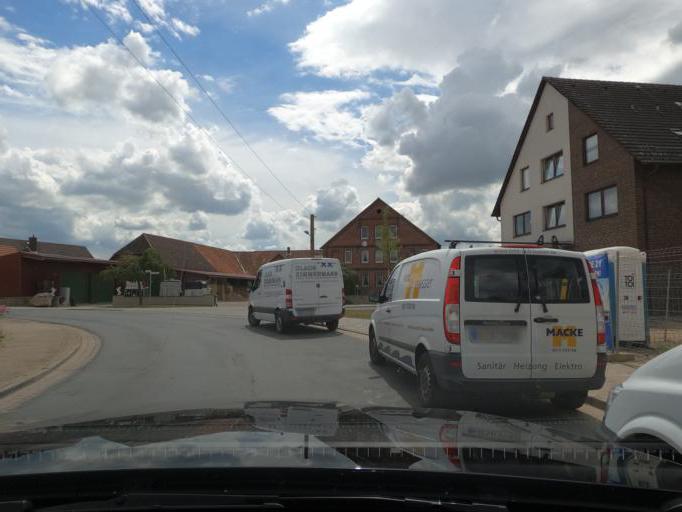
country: DE
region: Lower Saxony
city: Sehnde
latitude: 52.3394
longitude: 9.9116
